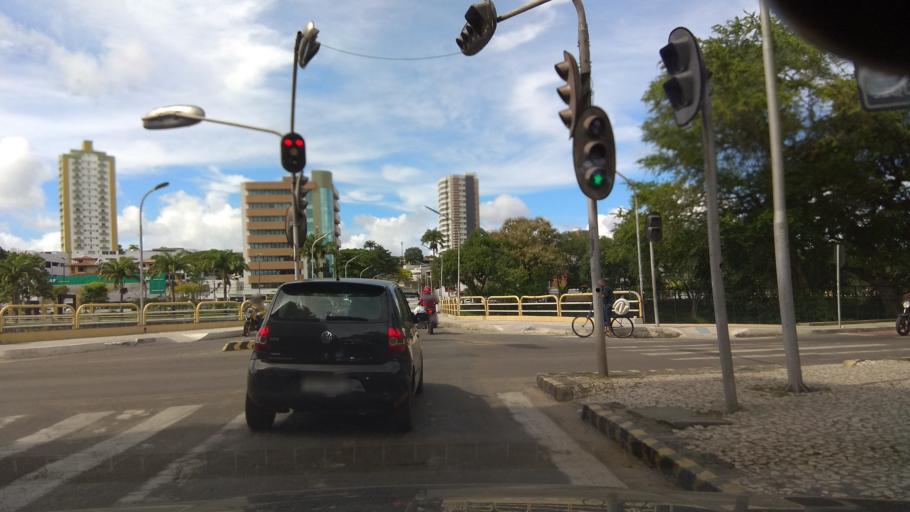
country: BR
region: Bahia
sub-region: Itabuna
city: Itabuna
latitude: -14.7929
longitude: -39.2747
